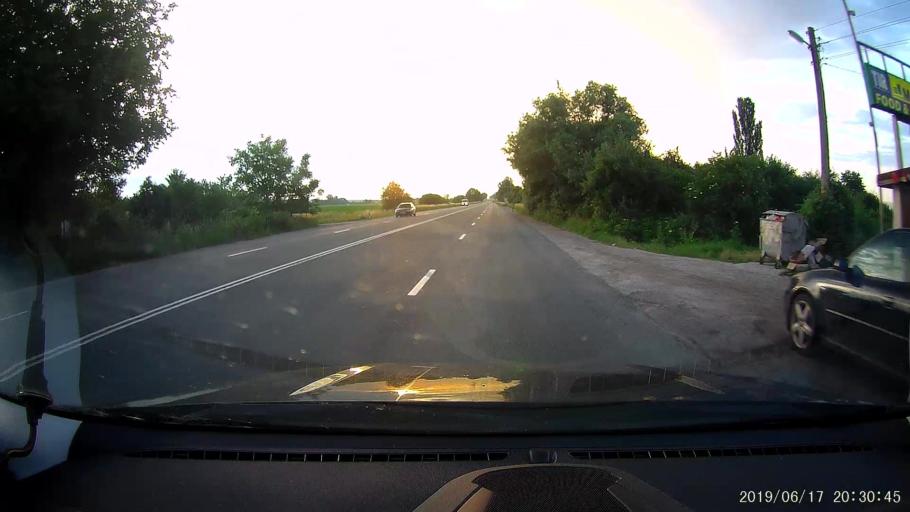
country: BG
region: Sofiya
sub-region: Obshtina Bozhurishte
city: Bozhurishte
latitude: 42.7968
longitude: 23.1434
